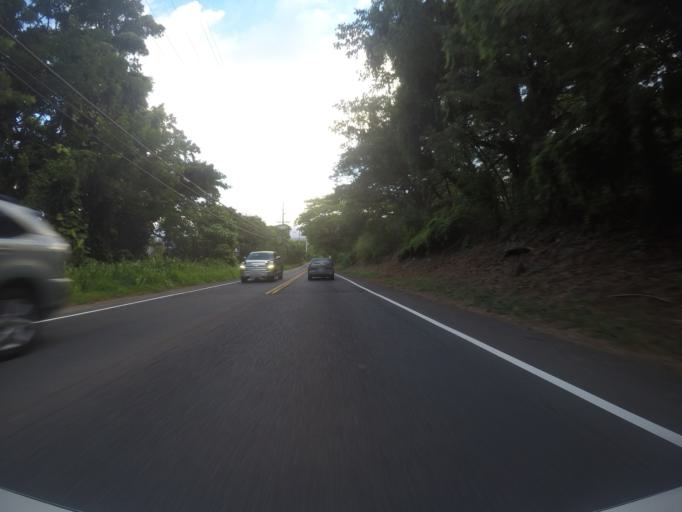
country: US
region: Hawaii
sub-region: Honolulu County
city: Ka'a'awa
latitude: 21.5151
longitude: -157.8443
